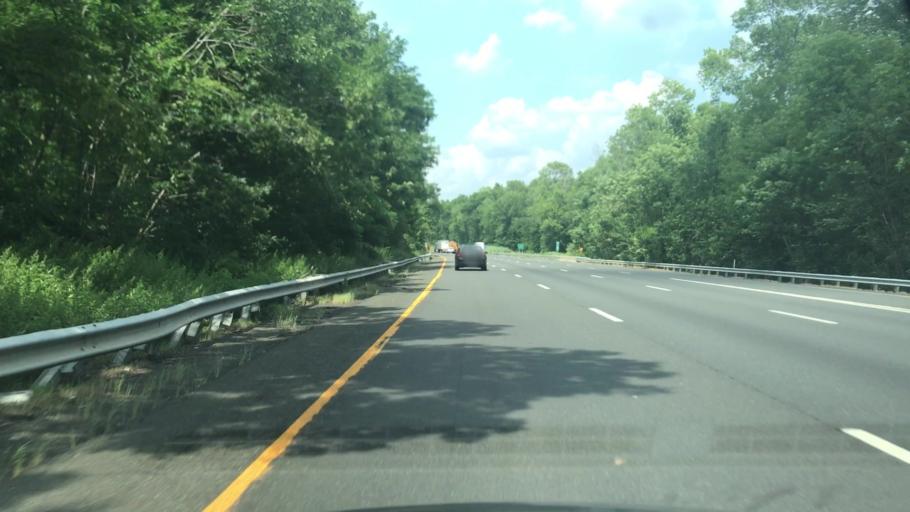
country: US
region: New Jersey
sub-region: Somerset County
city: Bernardsville
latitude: 40.7309
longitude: -74.5379
